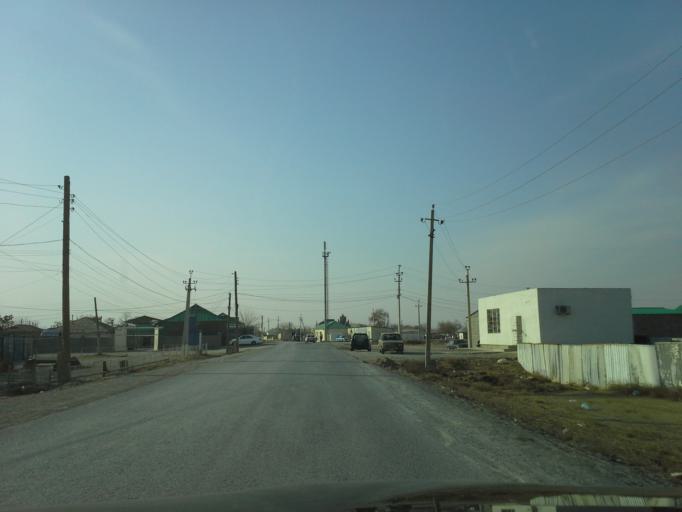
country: TM
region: Ahal
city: Abadan
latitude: 38.1729
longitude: 58.0455
